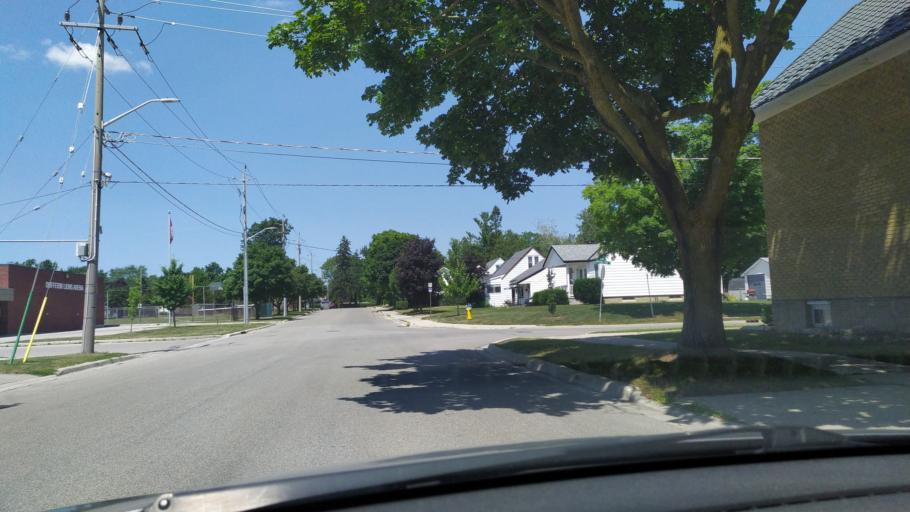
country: CA
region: Ontario
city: Stratford
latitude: 43.3577
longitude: -80.9859
